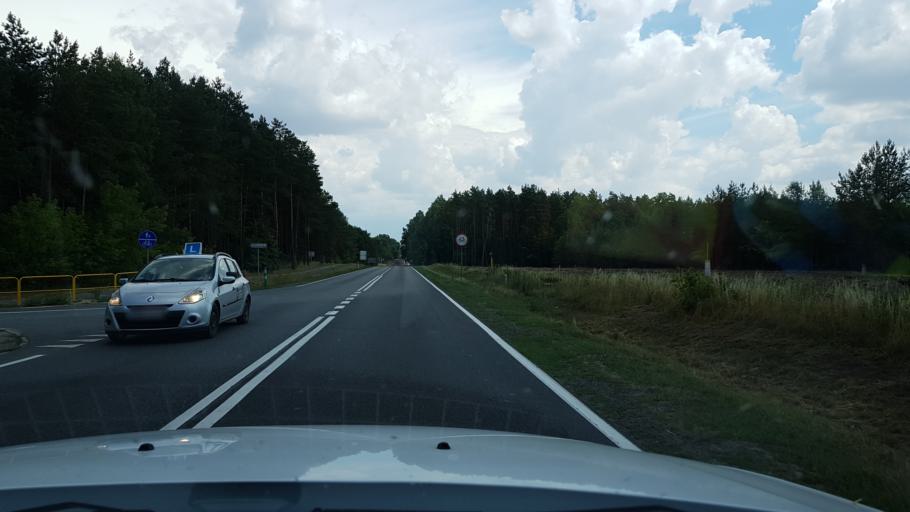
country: PL
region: West Pomeranian Voivodeship
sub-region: Powiat walecki
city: Walcz
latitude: 53.2931
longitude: 16.4287
